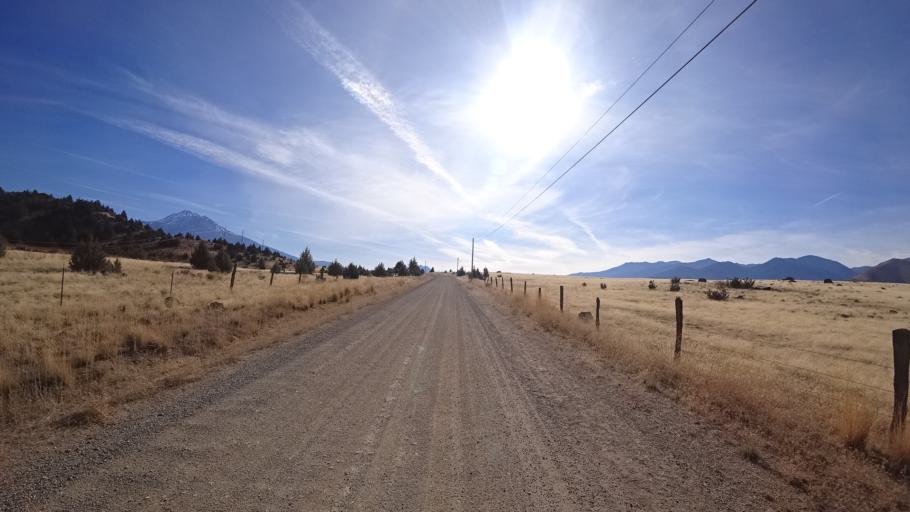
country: US
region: California
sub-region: Siskiyou County
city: Weed
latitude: 41.4927
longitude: -122.4513
